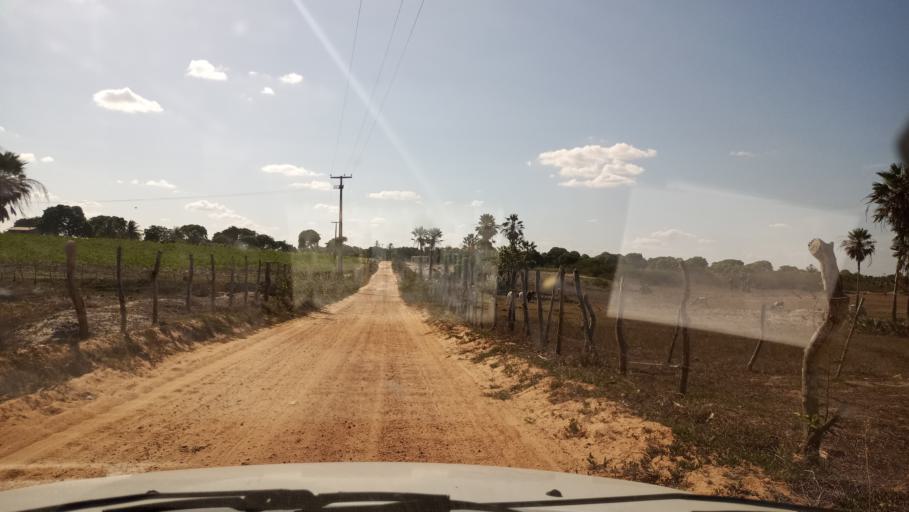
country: BR
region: Rio Grande do Norte
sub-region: Brejinho
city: Brejinho
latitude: -6.1765
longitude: -35.4597
